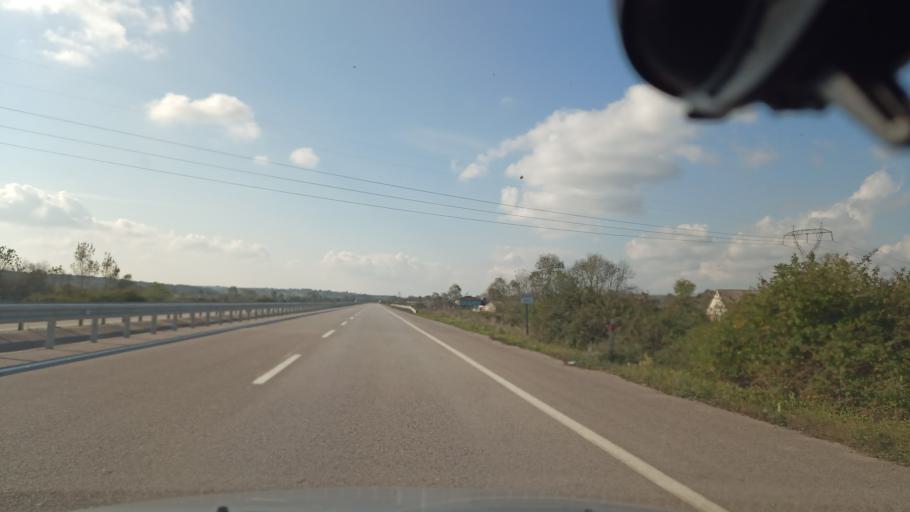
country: TR
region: Sakarya
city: Kaynarca
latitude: 41.0791
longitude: 30.4099
